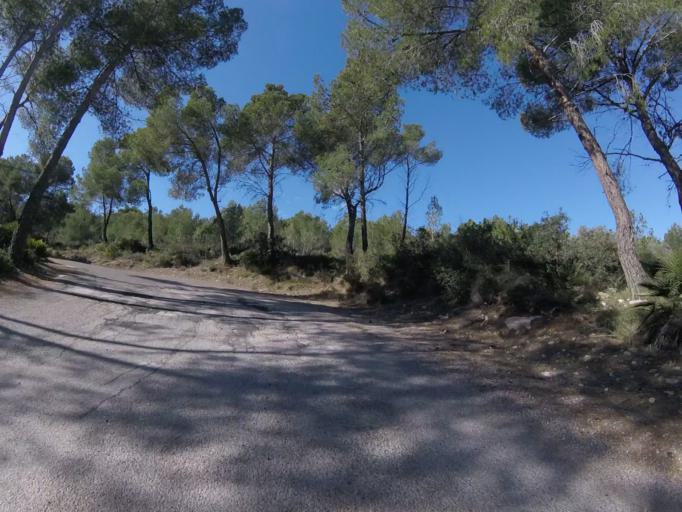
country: ES
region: Valencia
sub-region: Provincia de Castello
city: Orpesa/Oropesa del Mar
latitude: 40.0762
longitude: 0.1173
